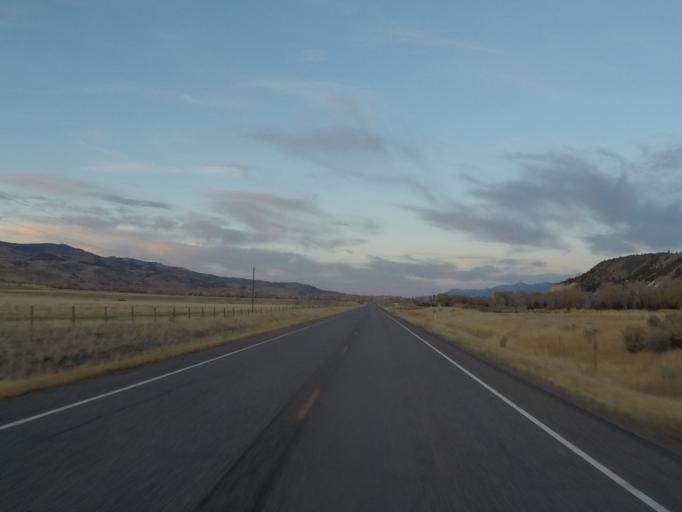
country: US
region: Montana
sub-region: Gallatin County
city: Bozeman
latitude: 45.2894
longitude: -110.8412
